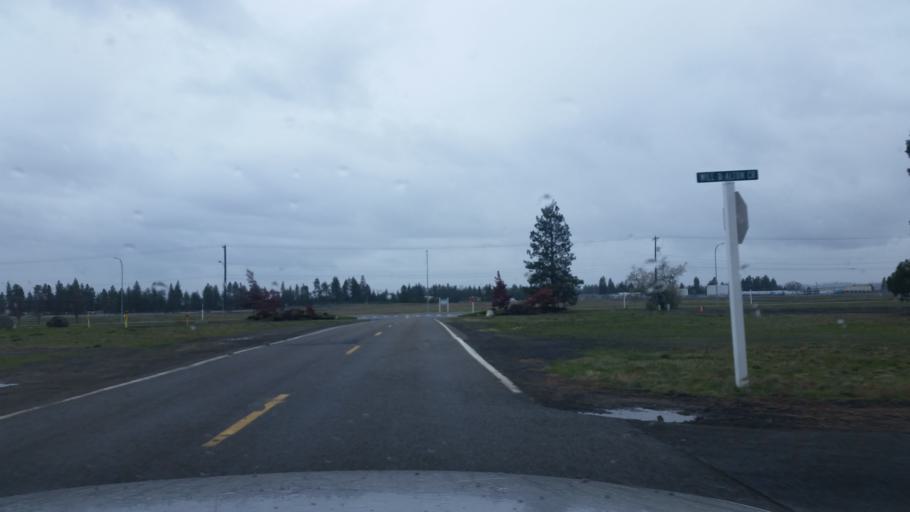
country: US
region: Washington
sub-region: Spokane County
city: Airway Heights
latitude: 47.6203
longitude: -117.5133
